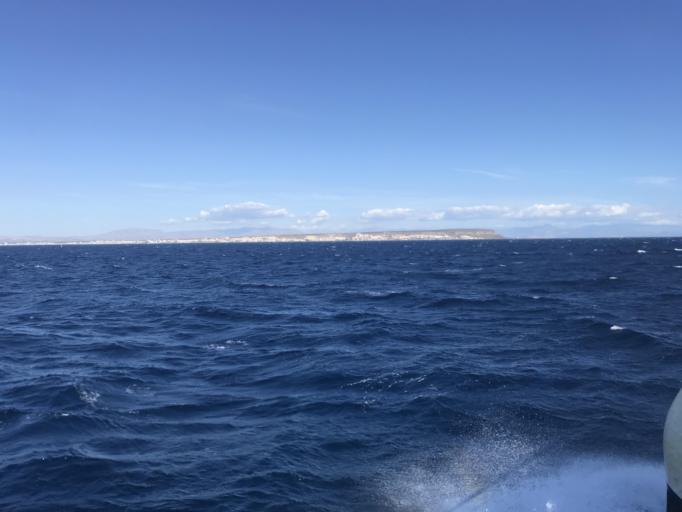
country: ES
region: Valencia
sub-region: Provincia de Alicante
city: Santa Pola
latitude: 38.1378
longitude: -0.5280
